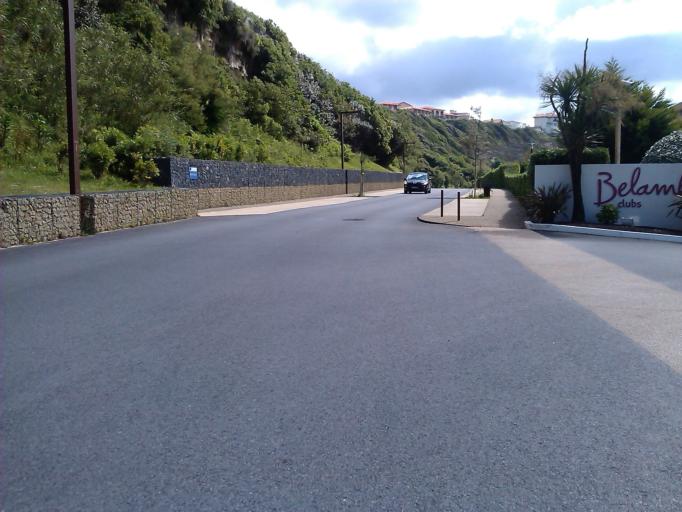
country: FR
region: Aquitaine
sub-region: Departement des Pyrenees-Atlantiques
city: Biarritz
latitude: 43.4969
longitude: -1.5432
